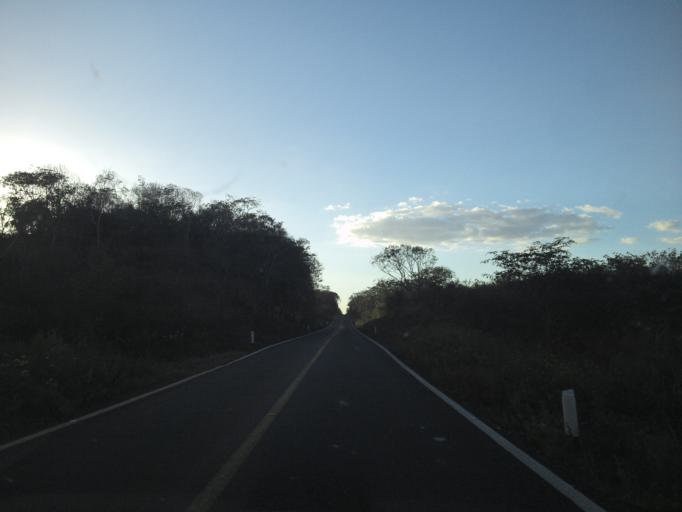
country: MX
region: Yucatan
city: Santa Elena
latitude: 20.3355
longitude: -89.6760
